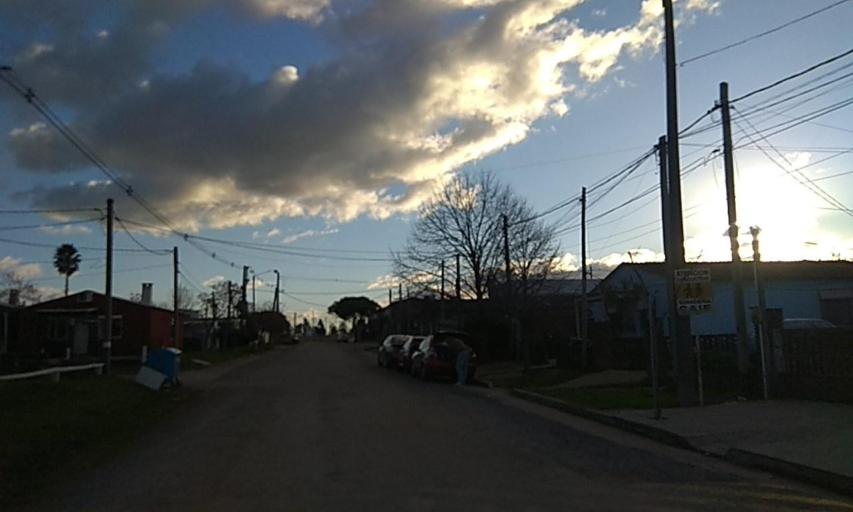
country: UY
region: Florida
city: Florida
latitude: -34.1047
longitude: -56.2295
